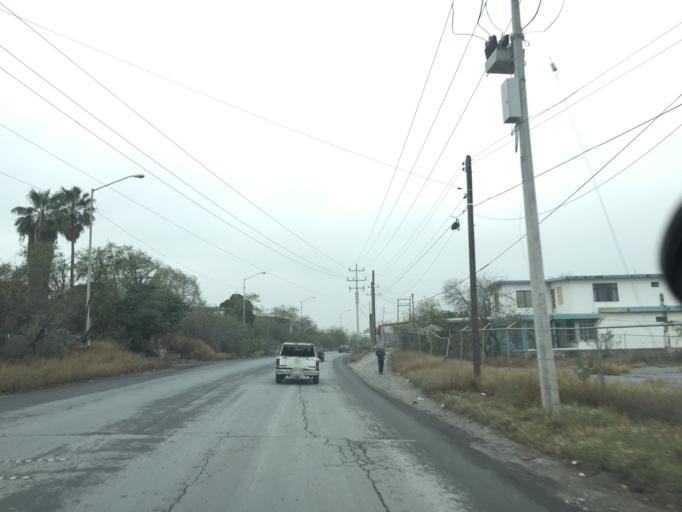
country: MX
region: Nuevo Leon
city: Mina
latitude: 25.9800
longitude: -100.4494
